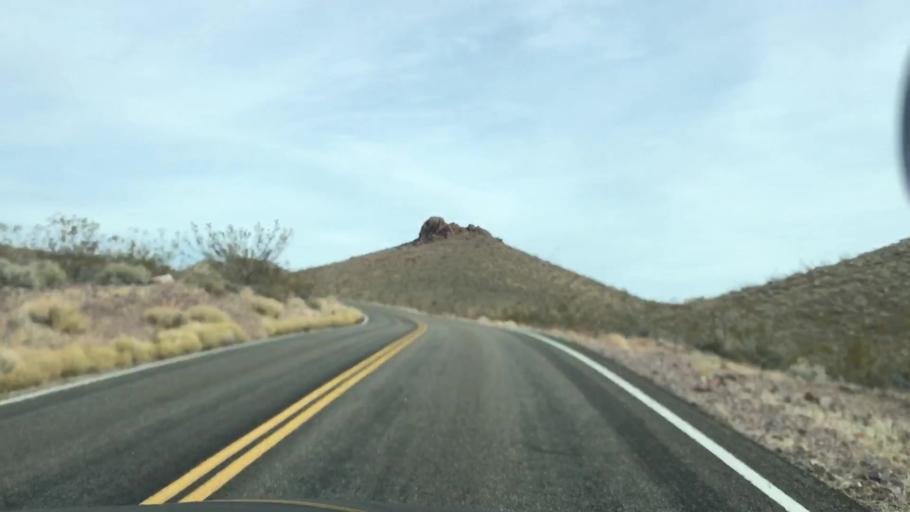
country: US
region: Nevada
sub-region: Nye County
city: Beatty
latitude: 36.7841
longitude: -116.9312
